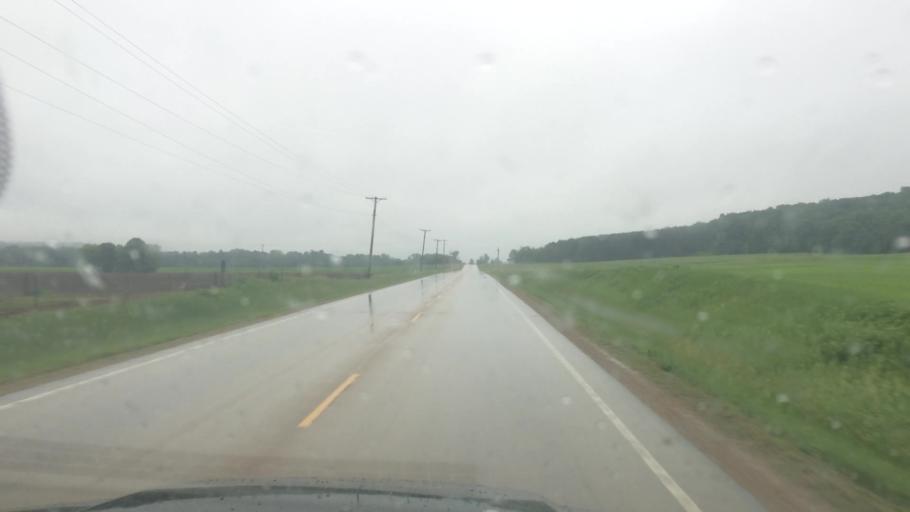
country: US
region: Wisconsin
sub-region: Waupaca County
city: Marion
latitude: 44.6103
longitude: -88.8936
